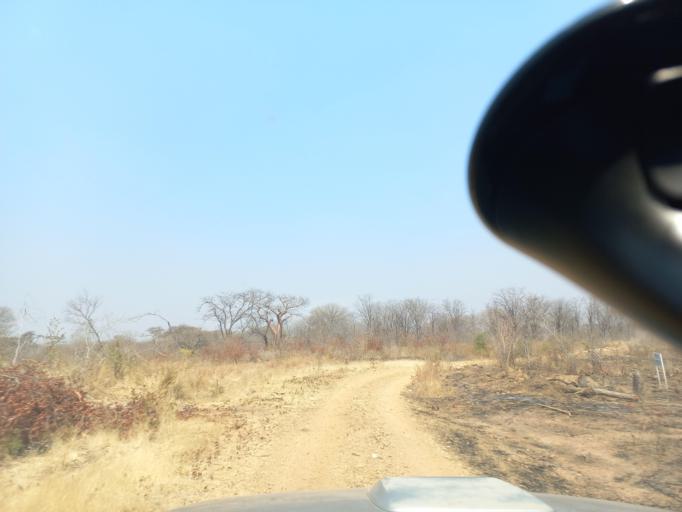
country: ZW
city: Chirundu
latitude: -15.8905
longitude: 28.7079
